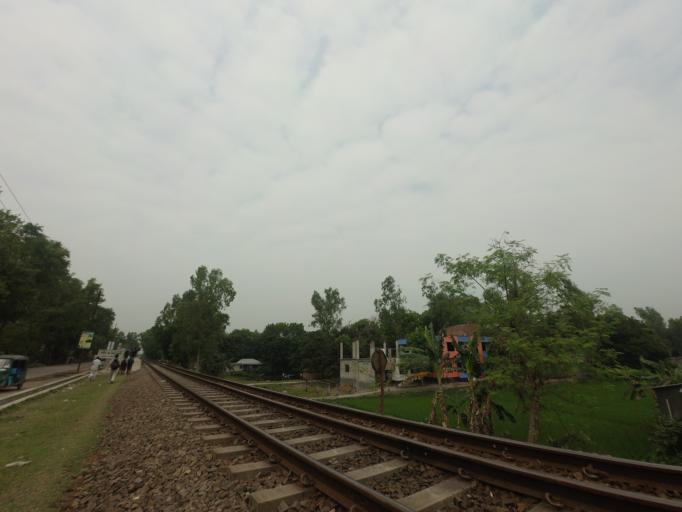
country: BD
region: Rajshahi
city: Sirajganj
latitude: 24.3968
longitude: 89.6921
